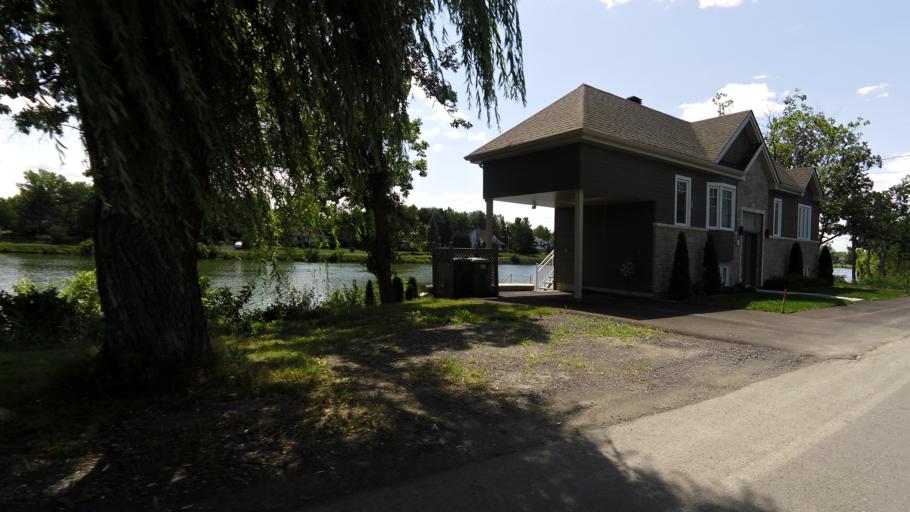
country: CA
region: Quebec
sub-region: Monteregie
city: Saint-Jean-sur-Richelieu
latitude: 45.3736
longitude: -73.2588
